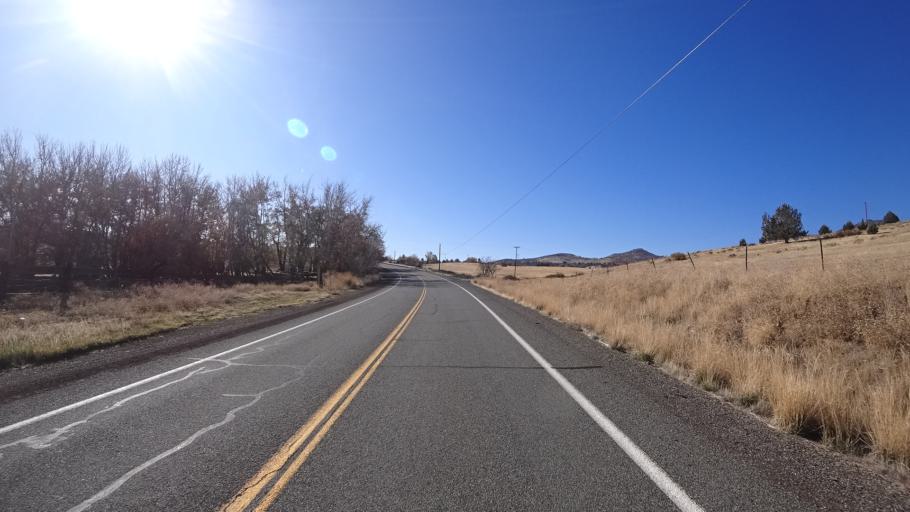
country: US
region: California
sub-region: Siskiyou County
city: Montague
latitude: 41.8195
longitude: -122.4962
